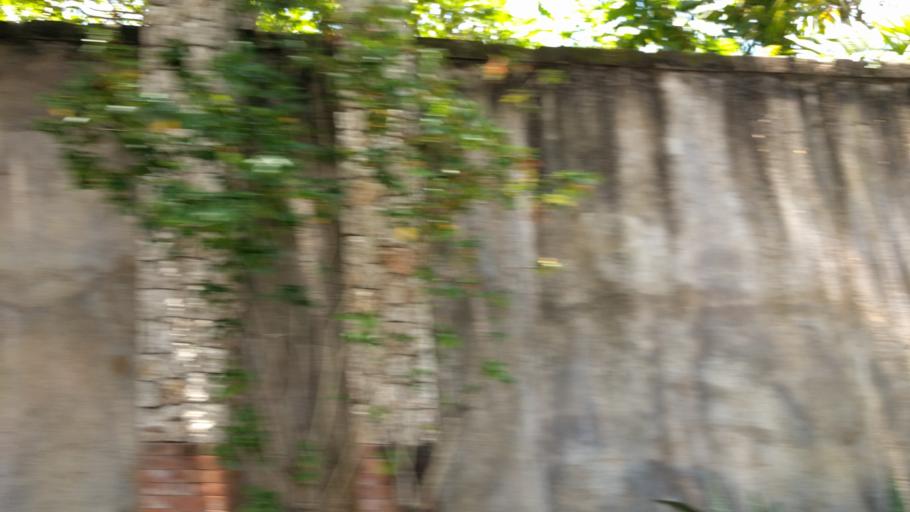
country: ID
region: Bali
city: Banjar Medura
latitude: -8.7055
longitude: 115.2505
